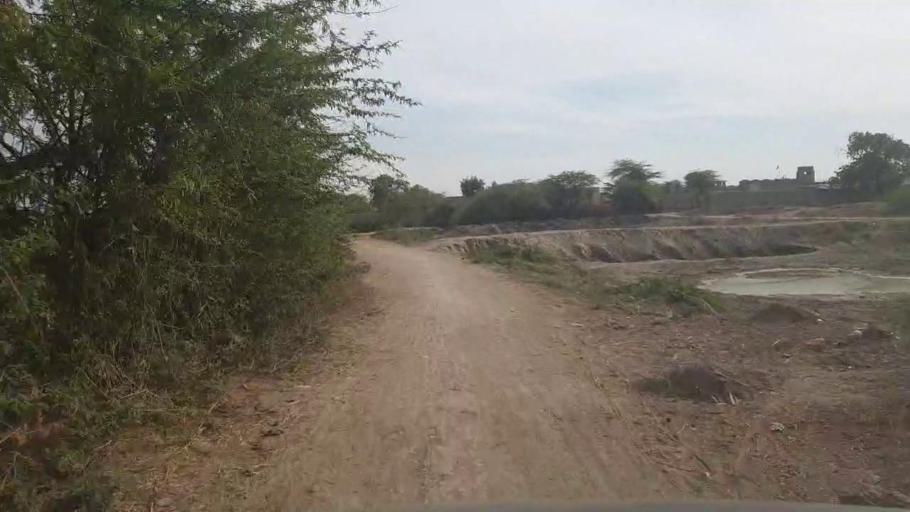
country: PK
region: Sindh
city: Kunri
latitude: 25.2963
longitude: 69.5890
